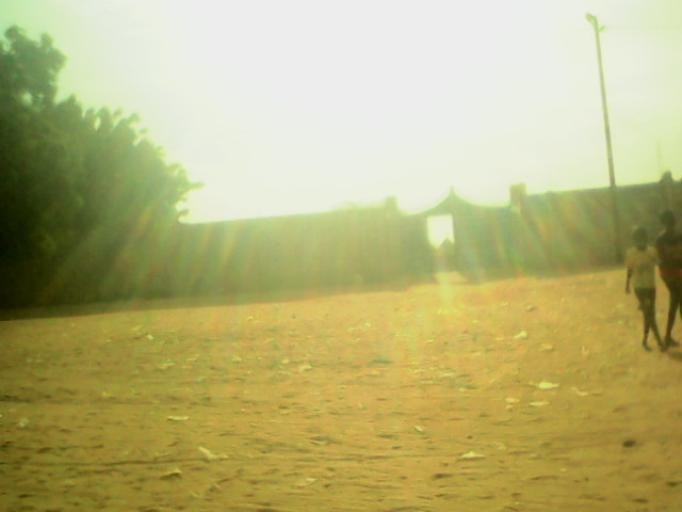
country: SN
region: Diourbel
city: Touba
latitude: 14.8584
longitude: -15.8947
